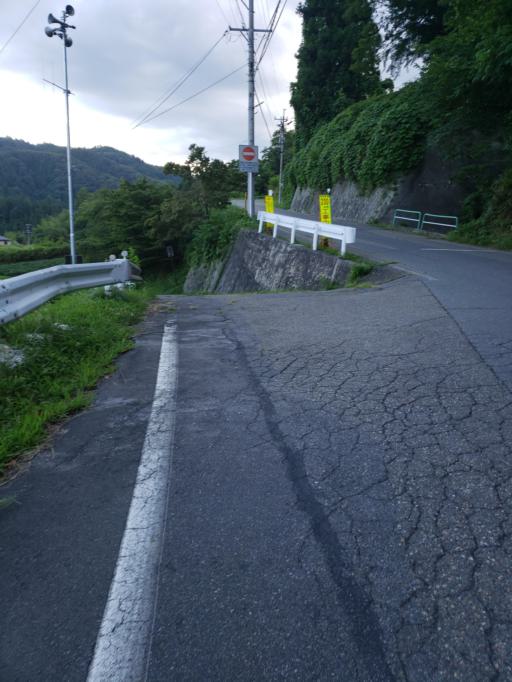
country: JP
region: Nagano
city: Nagano-shi
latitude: 36.6103
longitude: 138.0338
